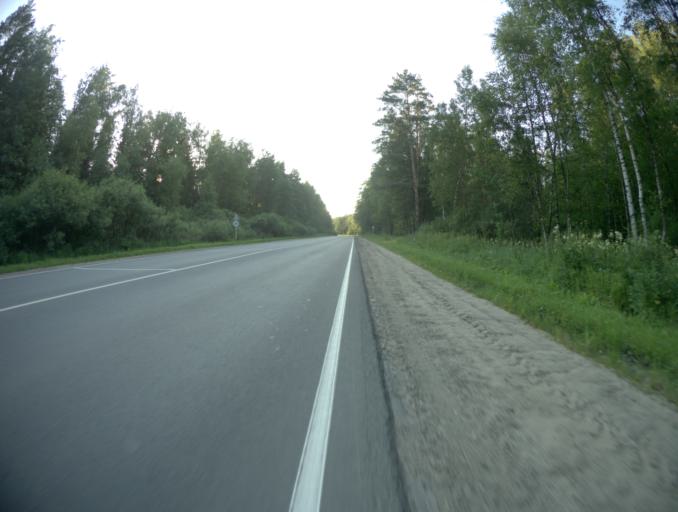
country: RU
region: Vladimir
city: Kommunar
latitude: 56.0573
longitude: 40.5177
